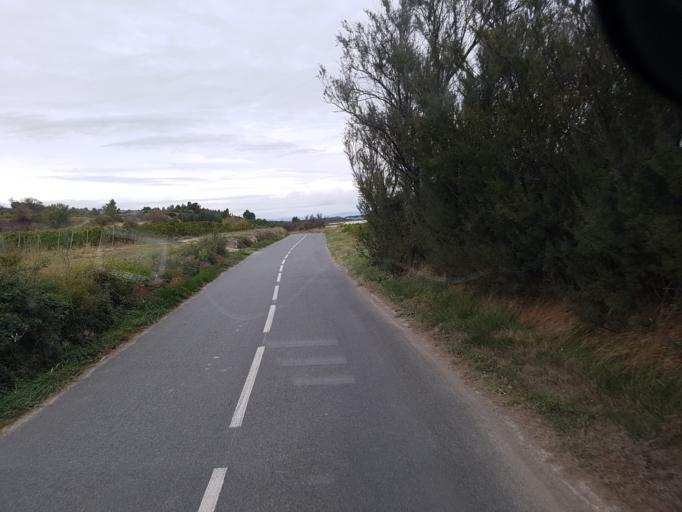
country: FR
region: Languedoc-Roussillon
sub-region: Departement de l'Aude
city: Peyriac-de-Mer
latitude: 43.1274
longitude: 2.9870
